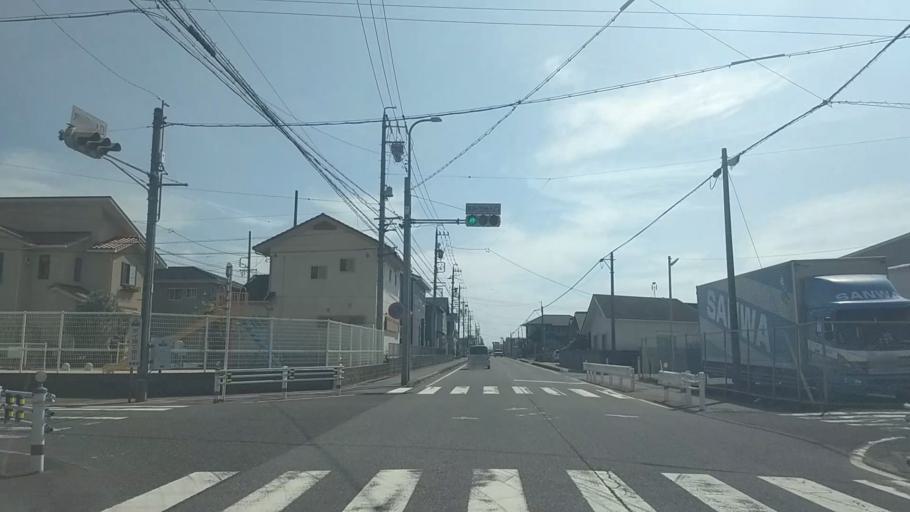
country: JP
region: Aichi
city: Anjo
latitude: 34.9721
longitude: 137.1077
